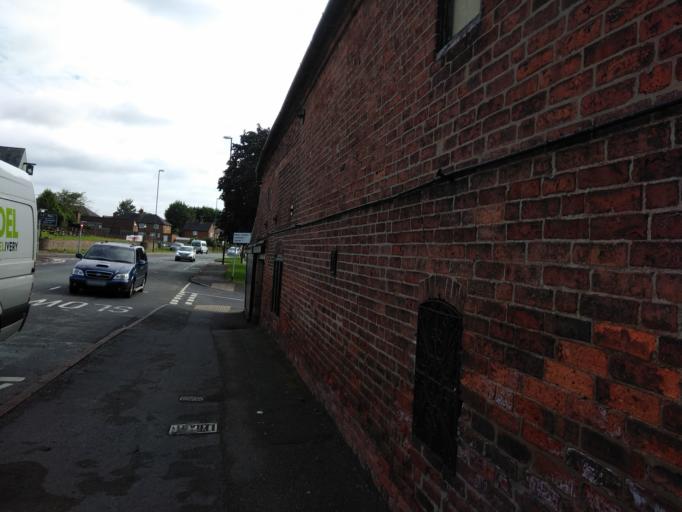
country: GB
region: England
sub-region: Nottinghamshire
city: Kimberley
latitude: 52.9731
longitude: -1.2272
